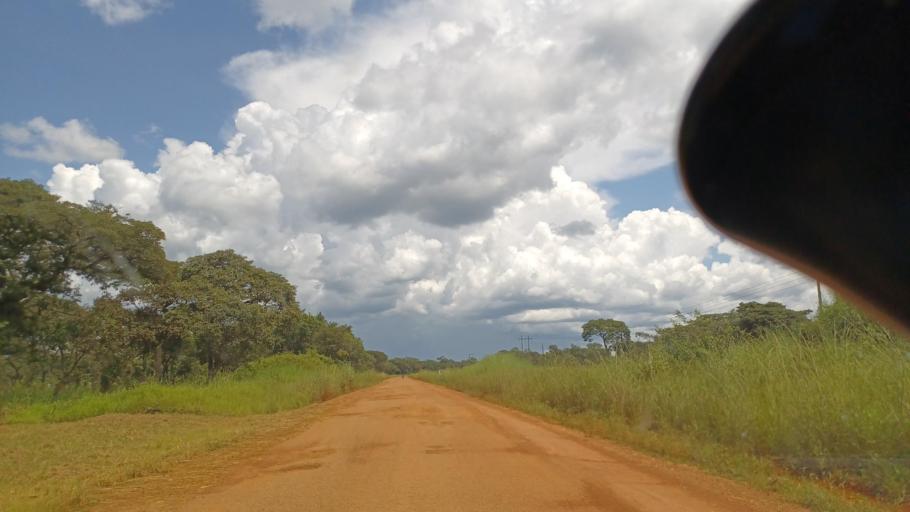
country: ZM
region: North-Western
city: Solwezi
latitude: -12.6910
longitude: 26.0403
